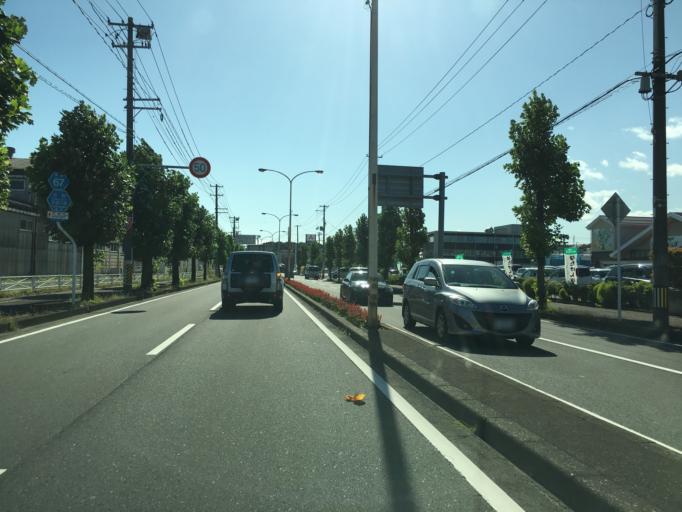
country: JP
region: Fukushima
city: Sukagawa
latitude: 37.2943
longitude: 140.3577
